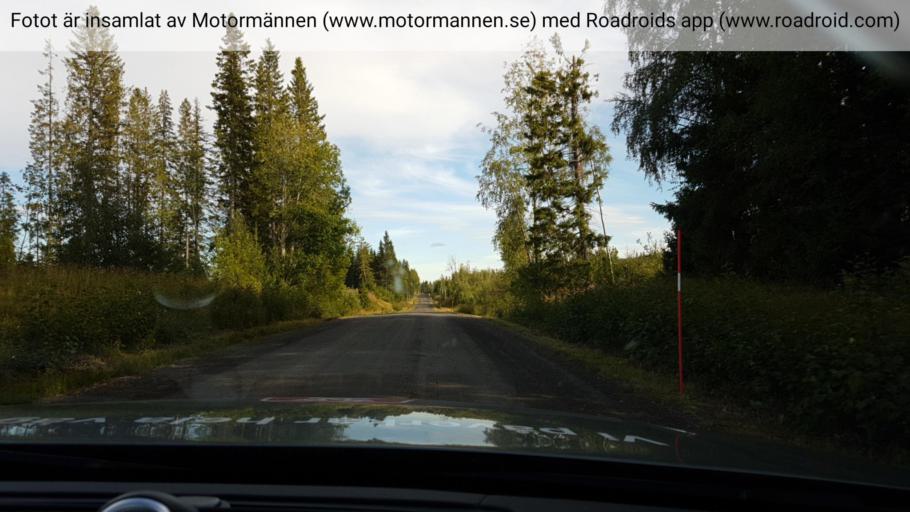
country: SE
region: Jaemtland
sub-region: Stroemsunds Kommun
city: Stroemsund
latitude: 64.1281
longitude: 15.7960
